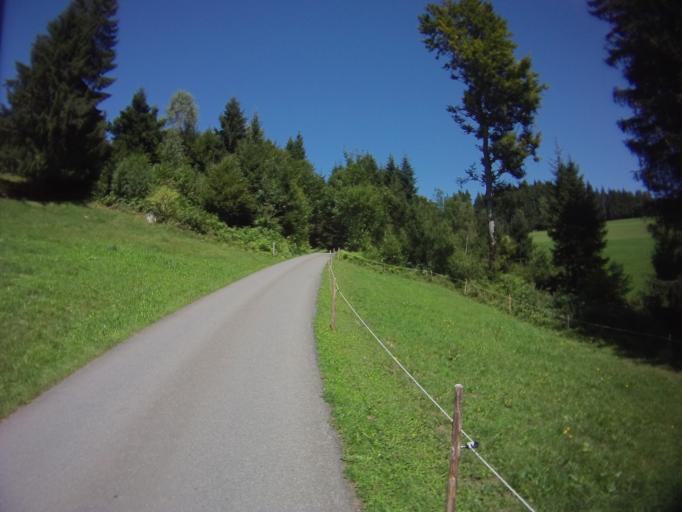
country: CH
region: Schwyz
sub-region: Bezirk Hoefe
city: Feusisberg
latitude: 47.1729
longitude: 8.7555
